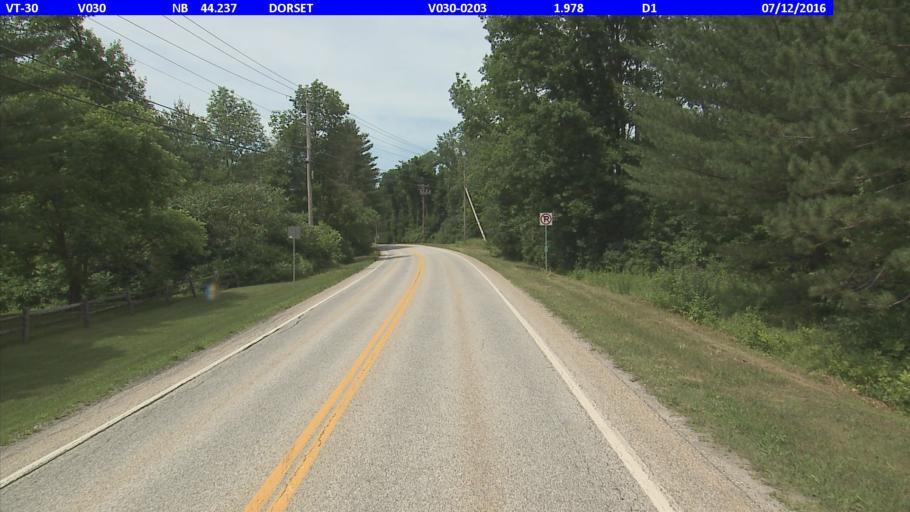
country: US
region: Vermont
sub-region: Bennington County
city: Manchester Center
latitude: 43.2377
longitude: -73.0849
